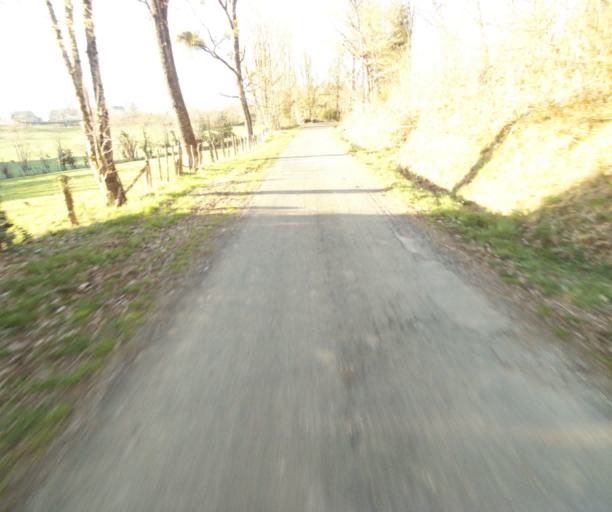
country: FR
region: Limousin
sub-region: Departement de la Correze
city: Saint-Clement
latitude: 45.3383
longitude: 1.7133
